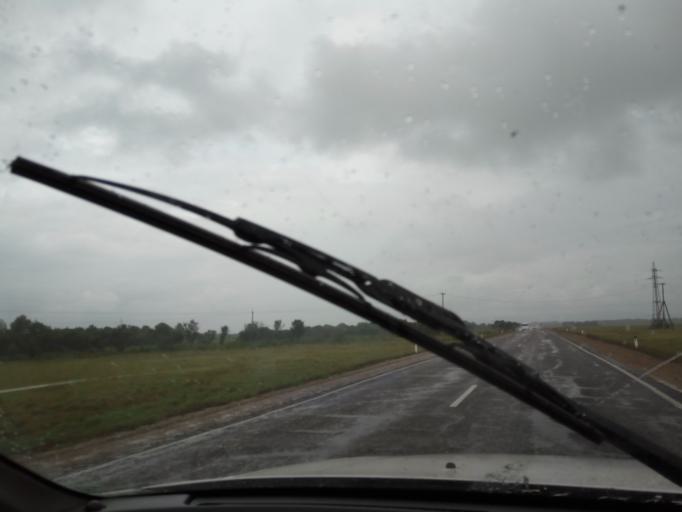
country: RU
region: Primorskiy
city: Dal'nerechensk
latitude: 45.9078
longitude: 133.7574
